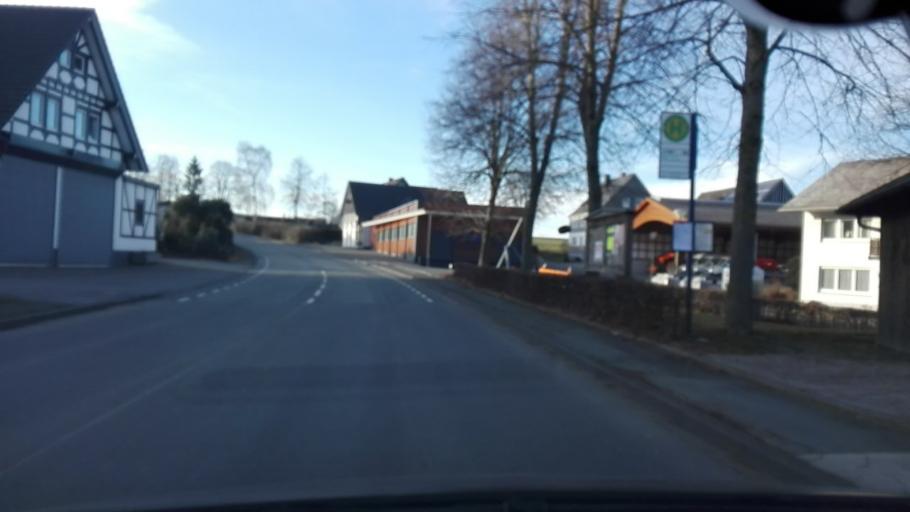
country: DE
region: North Rhine-Westphalia
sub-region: Regierungsbezirk Arnsberg
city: Schmallenberg
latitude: 51.1649
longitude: 8.2285
